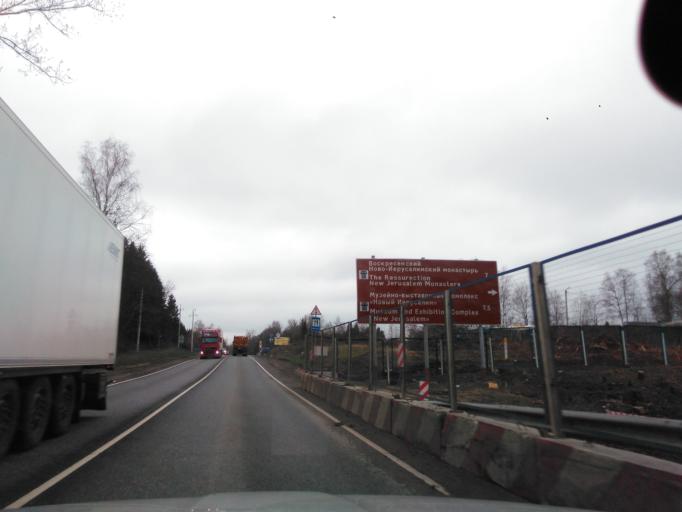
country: RU
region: Moskovskaya
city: Snegiri
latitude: 55.9310
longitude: 36.9528
